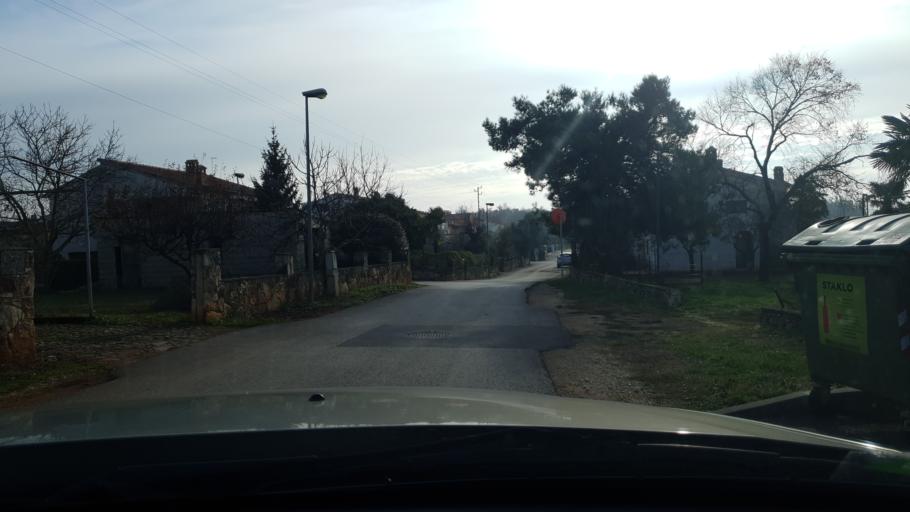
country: HR
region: Istarska
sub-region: Grad Porec
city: Porec
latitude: 45.2631
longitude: 13.6148
